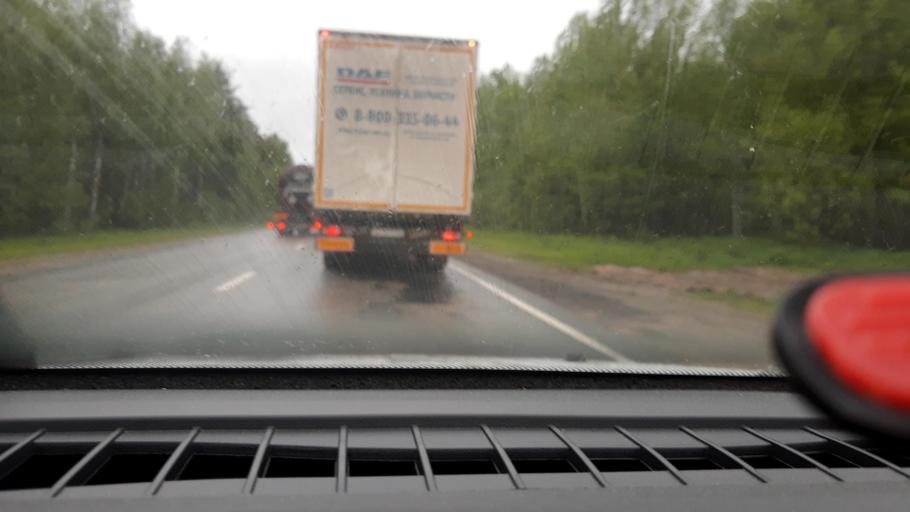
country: RU
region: Nizjnij Novgorod
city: Vladimirskoye
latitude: 56.9302
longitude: 45.0679
